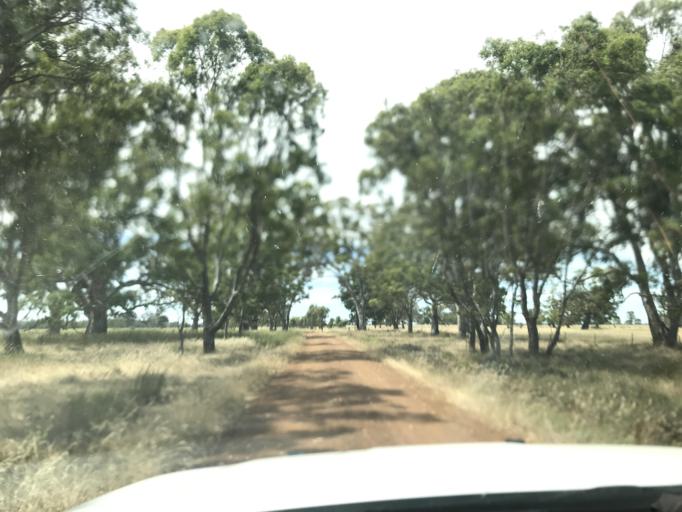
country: AU
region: South Australia
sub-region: Wattle Range
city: Penola
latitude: -37.0199
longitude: 141.4833
